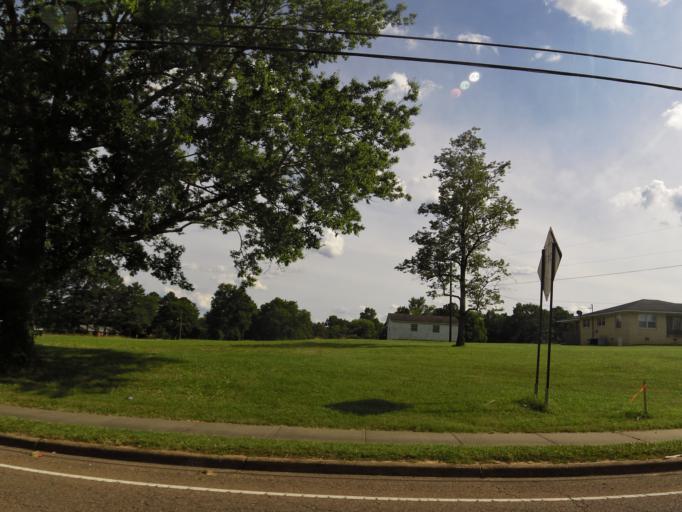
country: US
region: Tennessee
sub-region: Carroll County
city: Bruceton
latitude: 36.0381
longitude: -88.2393
